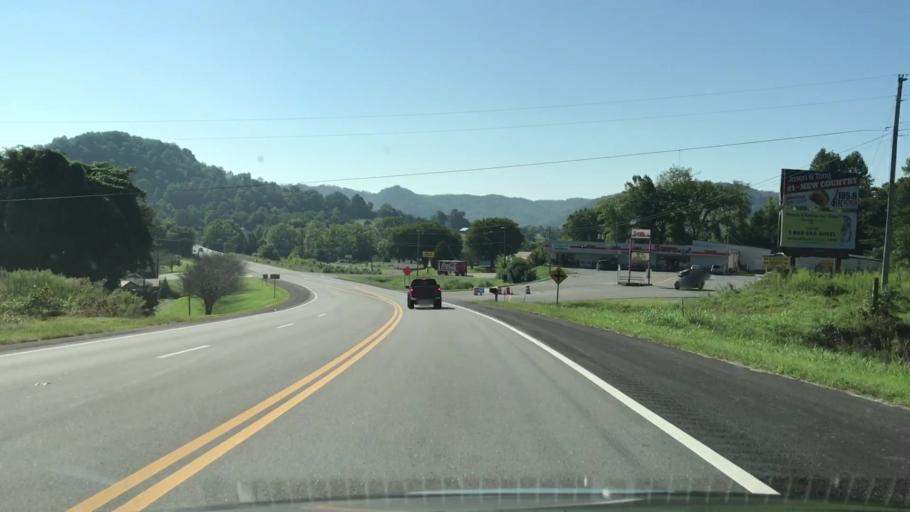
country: US
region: Tennessee
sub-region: Clay County
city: Celina
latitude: 36.5427
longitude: -85.4927
